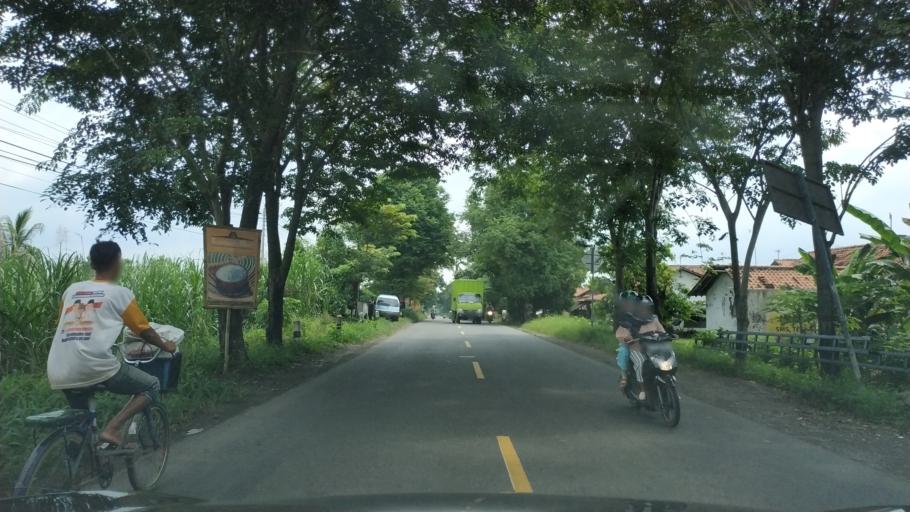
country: ID
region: Central Java
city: Lebaksiu
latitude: -7.0406
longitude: 109.1464
